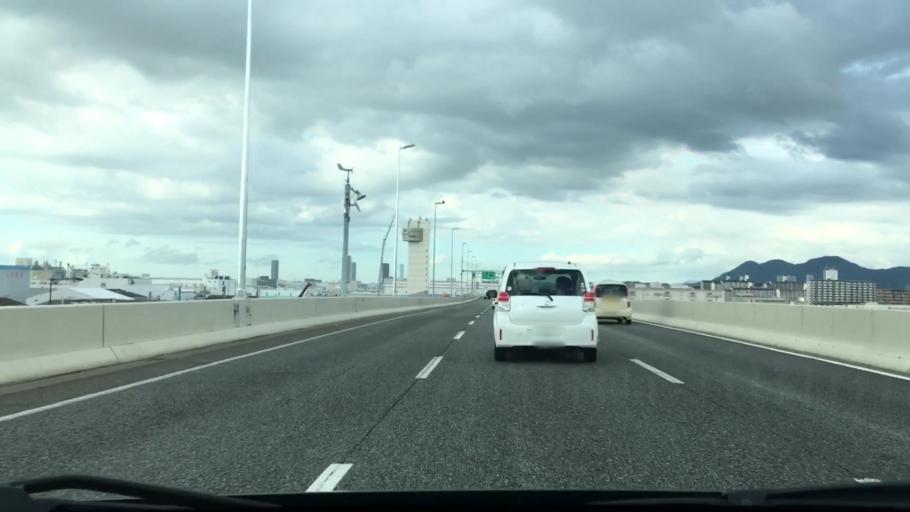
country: JP
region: Fukuoka
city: Fukuoka-shi
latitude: 33.6182
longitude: 130.4121
